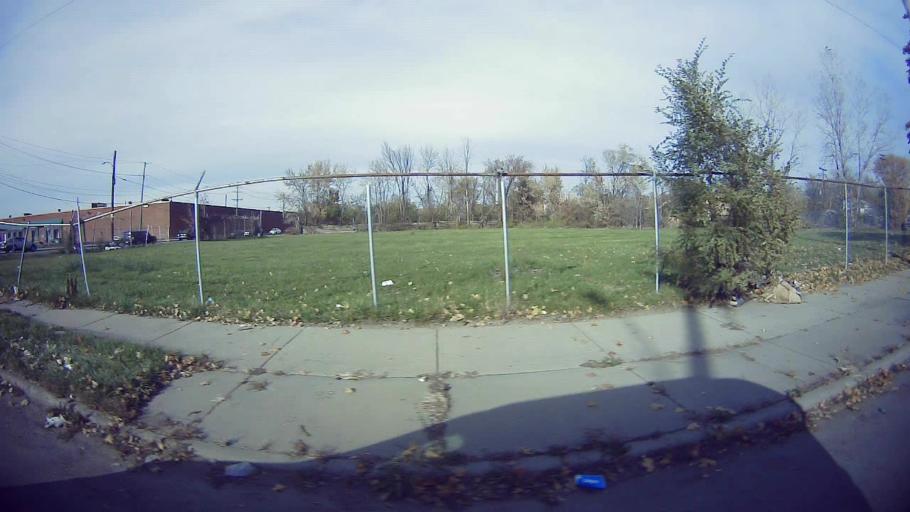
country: US
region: Michigan
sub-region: Wayne County
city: Dearborn
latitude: 42.3804
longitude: -83.1775
